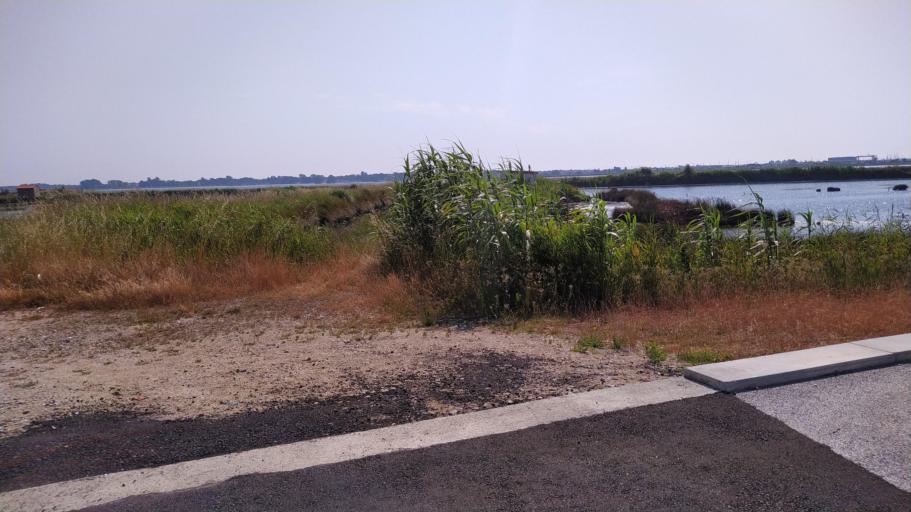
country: PT
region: Aveiro
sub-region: Aveiro
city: Aveiro
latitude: 40.6310
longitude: -8.6618
